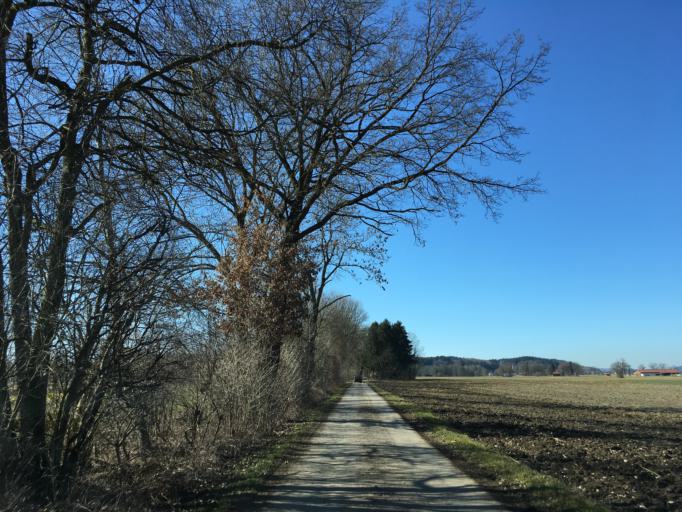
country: DE
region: Bavaria
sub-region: Upper Bavaria
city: Bad Aibling
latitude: 47.8366
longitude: 12.0029
